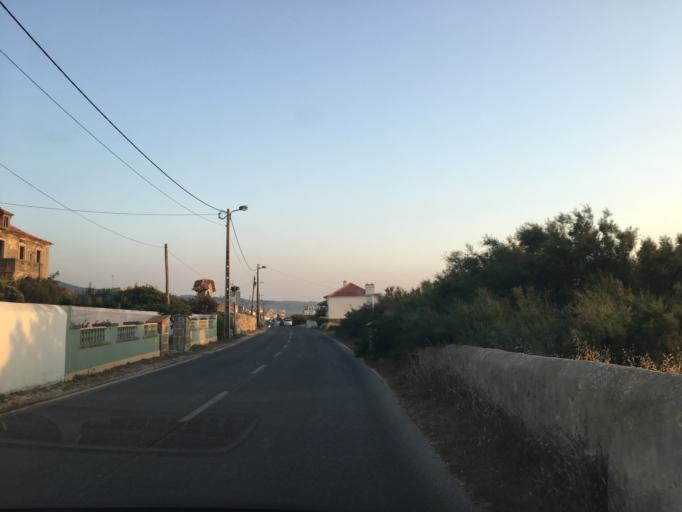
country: PT
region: Lisbon
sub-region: Sintra
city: Colares
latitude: 38.8355
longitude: -9.4659
